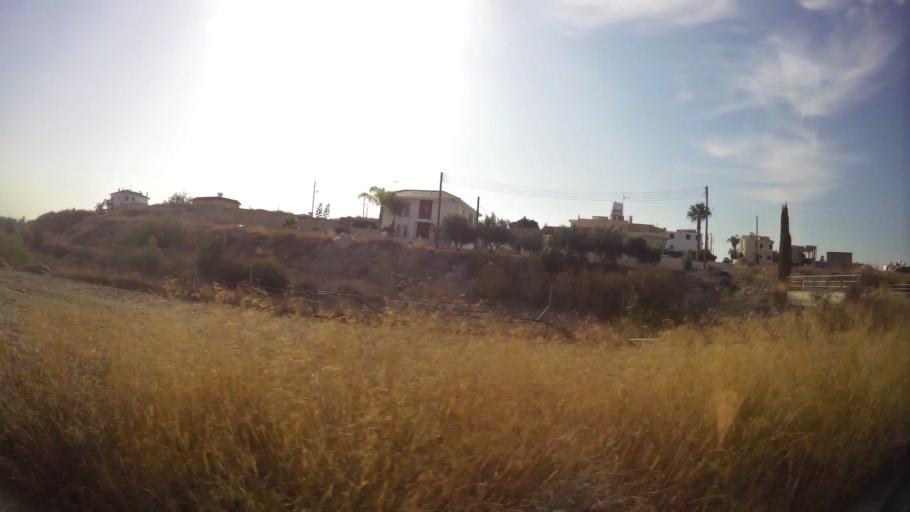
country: CY
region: Larnaka
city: Aradippou
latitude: 34.9555
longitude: 33.5950
